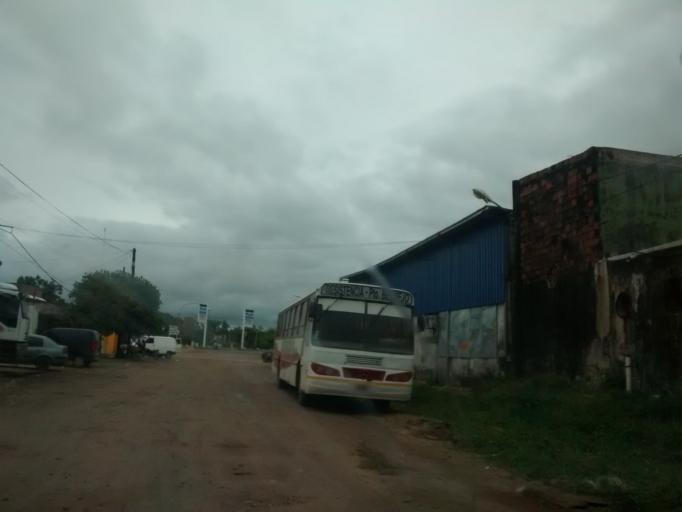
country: AR
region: Chaco
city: Fontana
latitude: -27.4351
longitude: -59.0063
